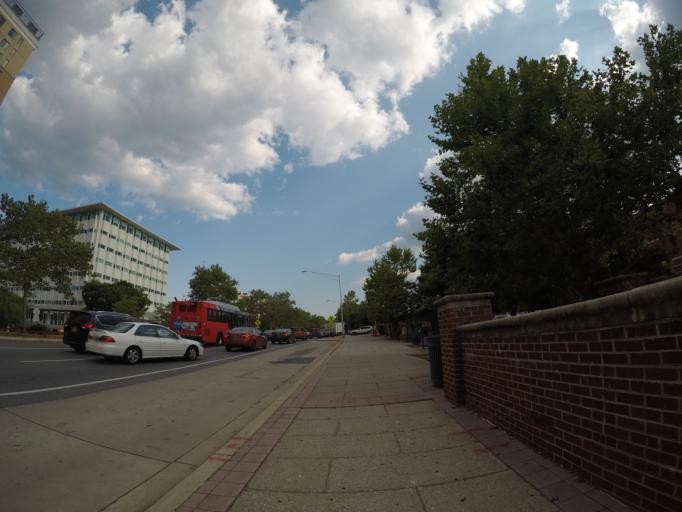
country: US
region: Maryland
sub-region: Prince George's County
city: University Park
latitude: 38.9685
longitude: -76.9542
